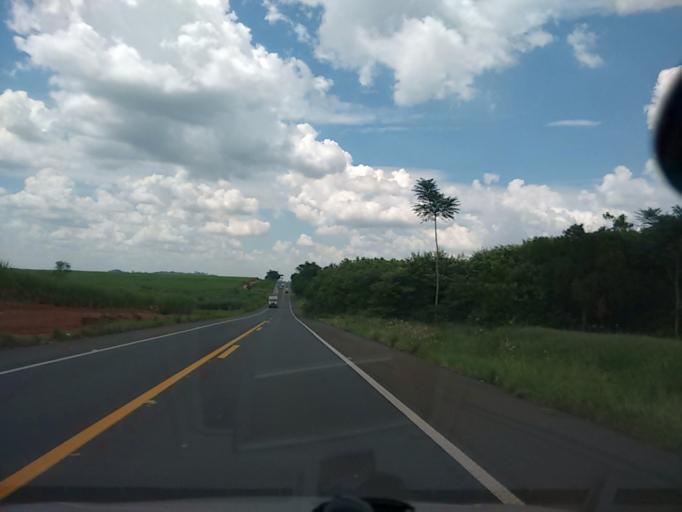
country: BR
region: Sao Paulo
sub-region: Osvaldo Cruz
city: Osvaldo Cruz
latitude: -21.8994
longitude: -50.8810
